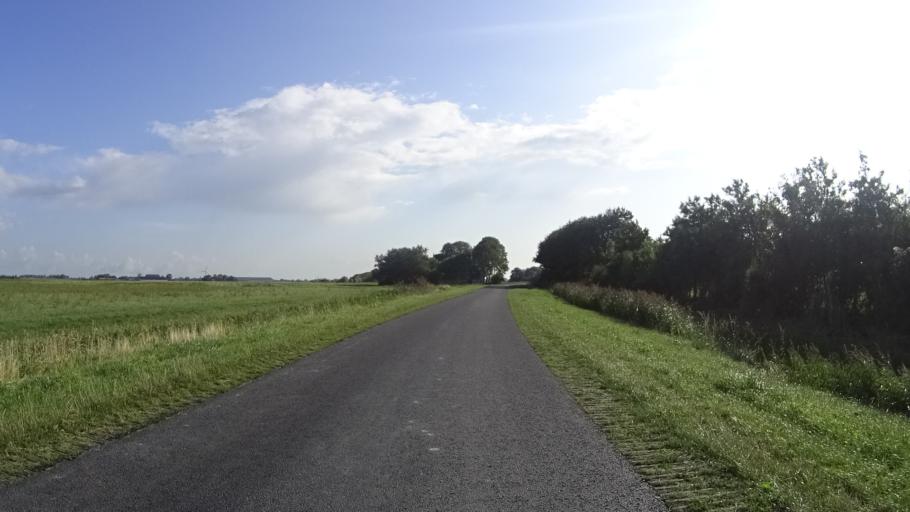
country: NL
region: Friesland
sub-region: Gemeente Harlingen
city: Harlingen
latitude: 53.1182
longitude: 5.4186
